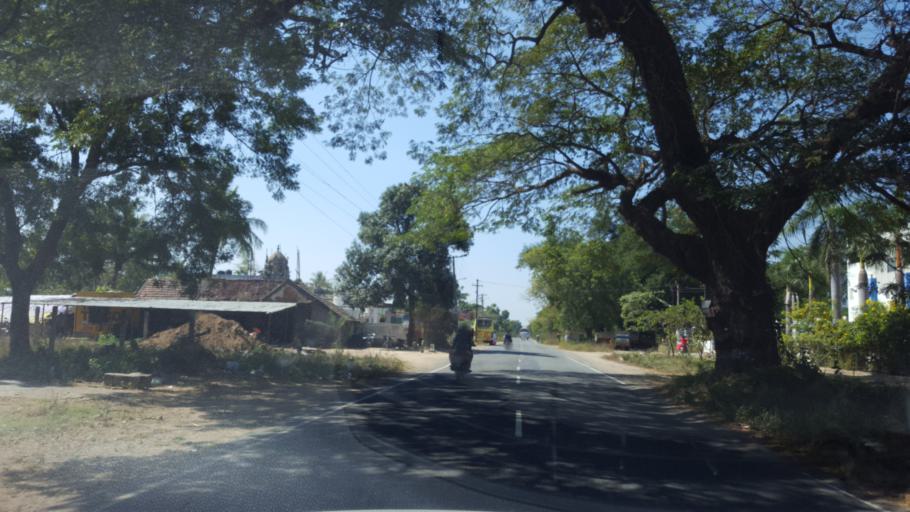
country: IN
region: Tamil Nadu
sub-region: Kancheepuram
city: Wallajahbad
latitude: 12.7650
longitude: 79.9073
